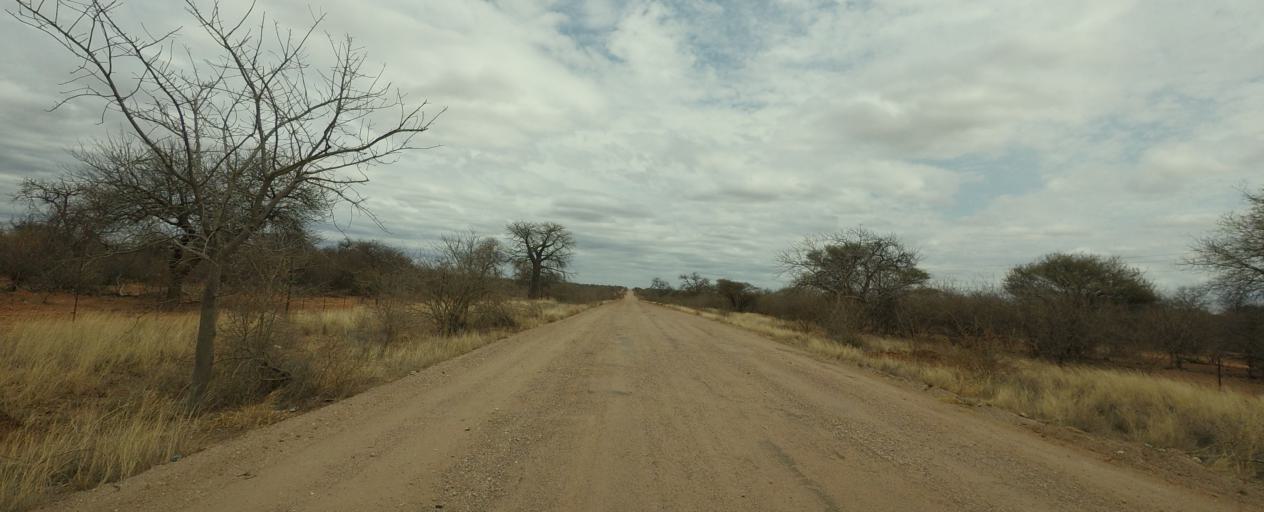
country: BW
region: Central
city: Mathathane
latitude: -22.6726
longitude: 28.6789
